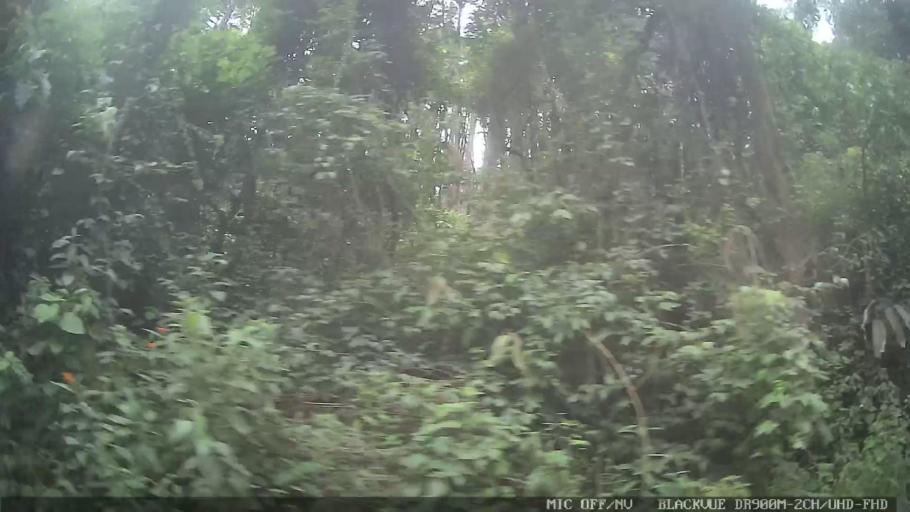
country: BR
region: Sao Paulo
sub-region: Bom Jesus Dos Perdoes
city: Bom Jesus dos Perdoes
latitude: -23.1654
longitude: -46.5109
